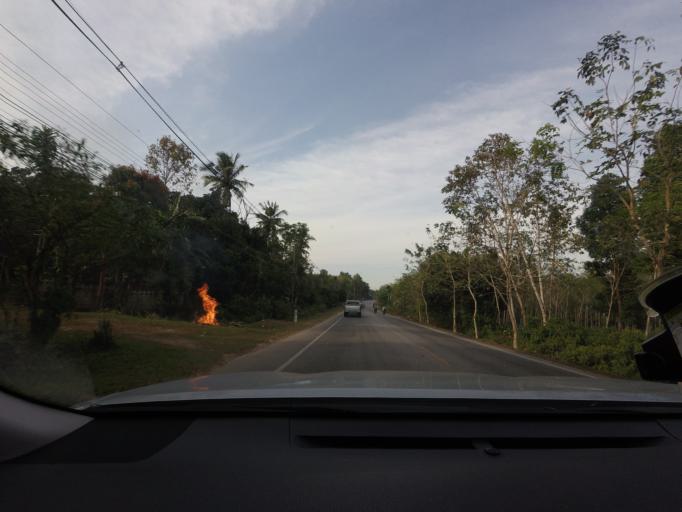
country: TH
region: Narathiwat
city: Ra-ngae
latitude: 6.3090
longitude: 101.7276
